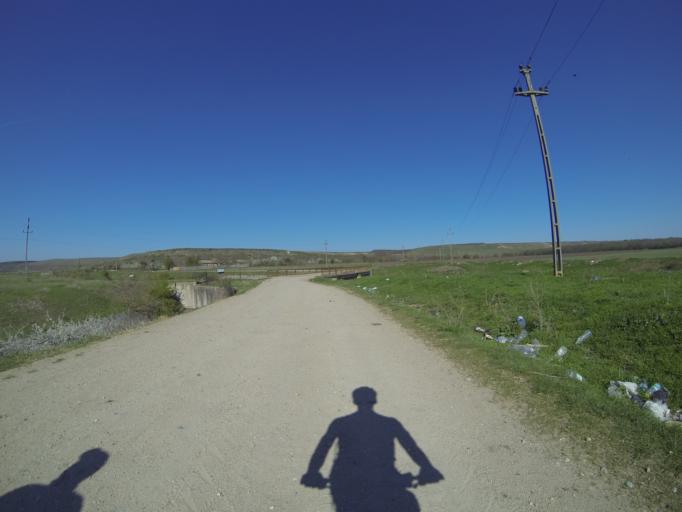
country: RO
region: Dolj
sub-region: Comuna Lipovu
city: Lipovu
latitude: 44.1203
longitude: 23.6180
